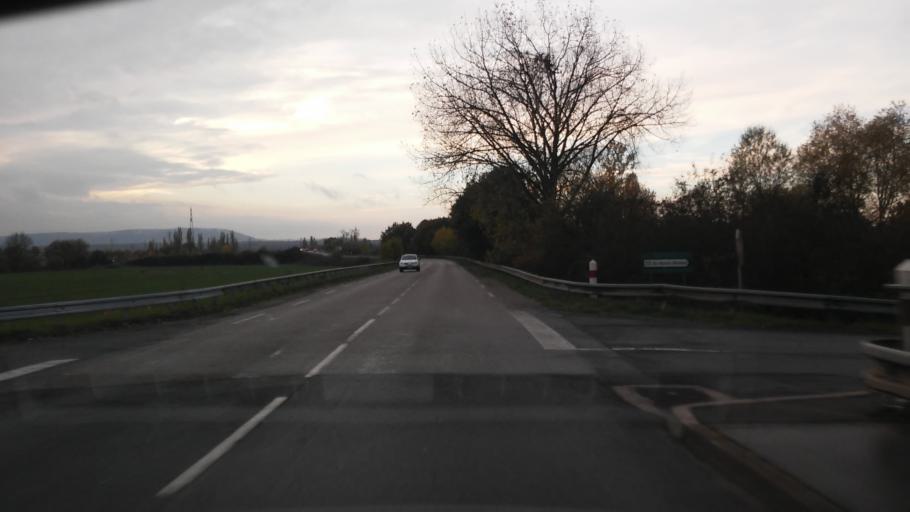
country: FR
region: Lorraine
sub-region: Departement de la Moselle
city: Talange
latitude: 49.2419
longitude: 6.1893
